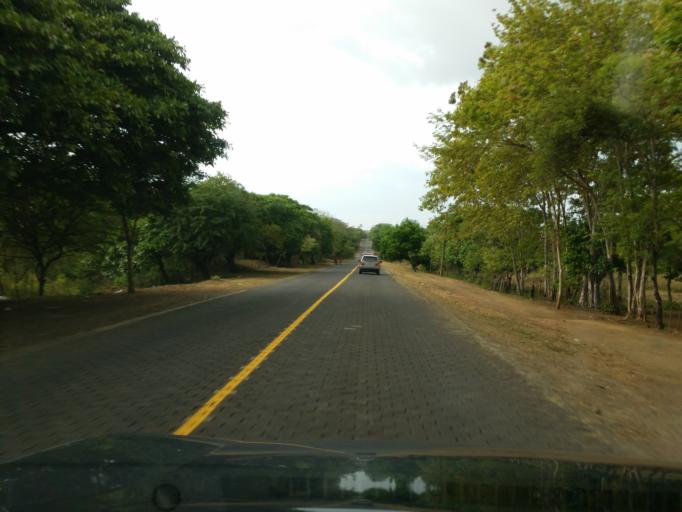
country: NI
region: Managua
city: Carlos Fonseca Amador
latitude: 11.9736
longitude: -86.5141
